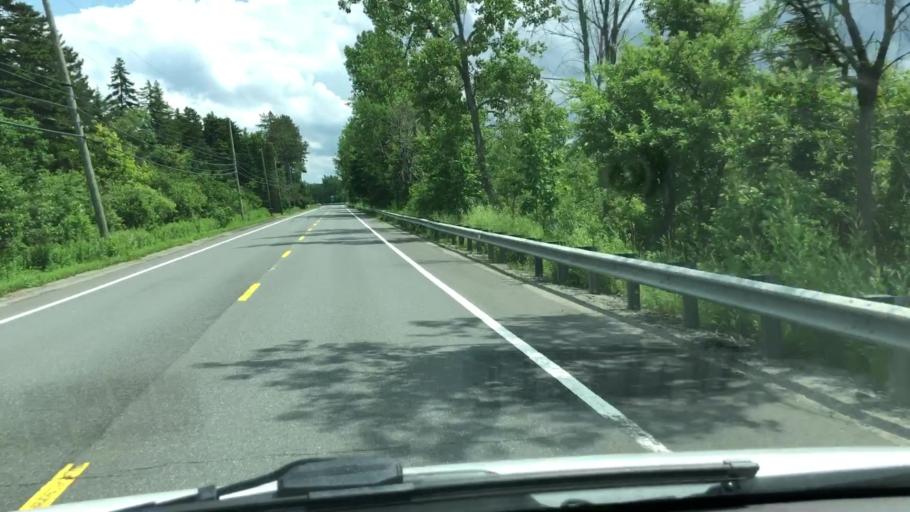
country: US
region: Massachusetts
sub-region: Berkshire County
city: Adams
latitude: 42.5728
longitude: -73.0449
